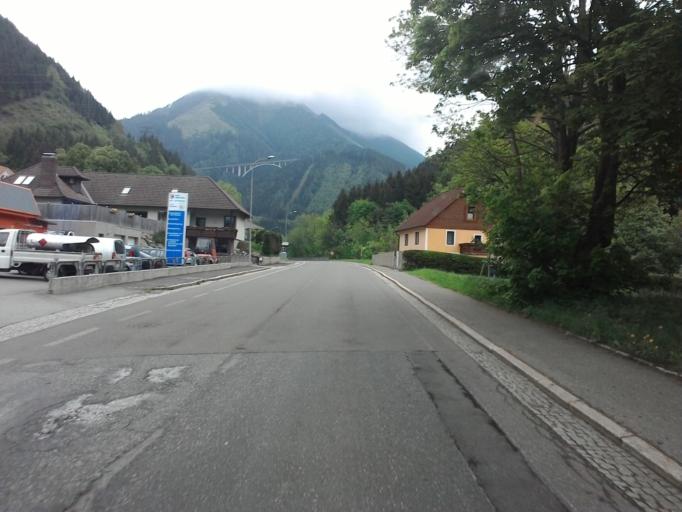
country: AT
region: Styria
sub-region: Politischer Bezirk Leoben
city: Eisenerz
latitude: 47.5414
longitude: 14.9070
